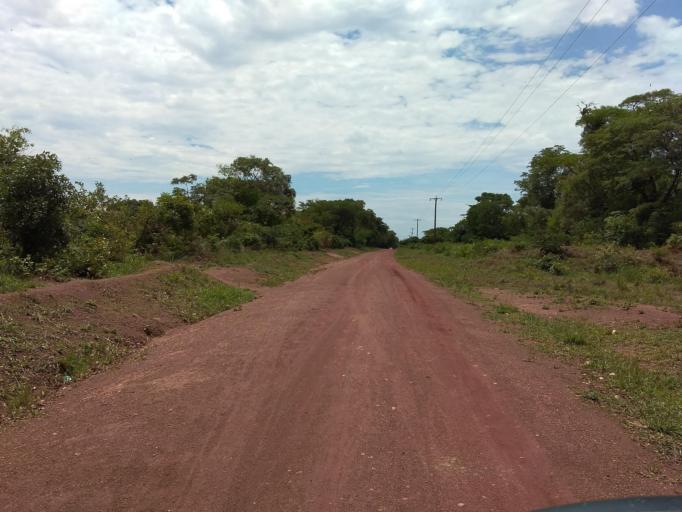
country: ZM
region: Central
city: Kapiri Mposhi
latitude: -13.4825
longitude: 28.7955
